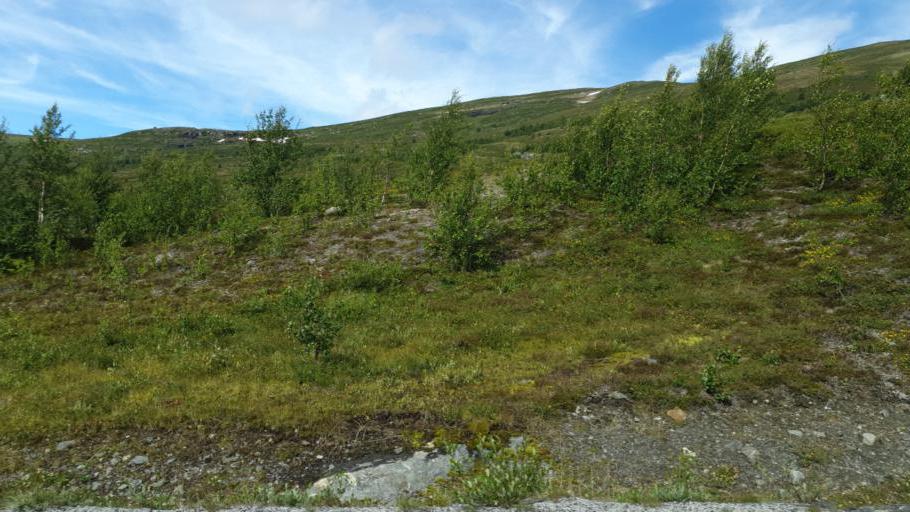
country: NO
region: Oppland
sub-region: Oystre Slidre
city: Heggenes
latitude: 61.5170
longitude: 8.8616
